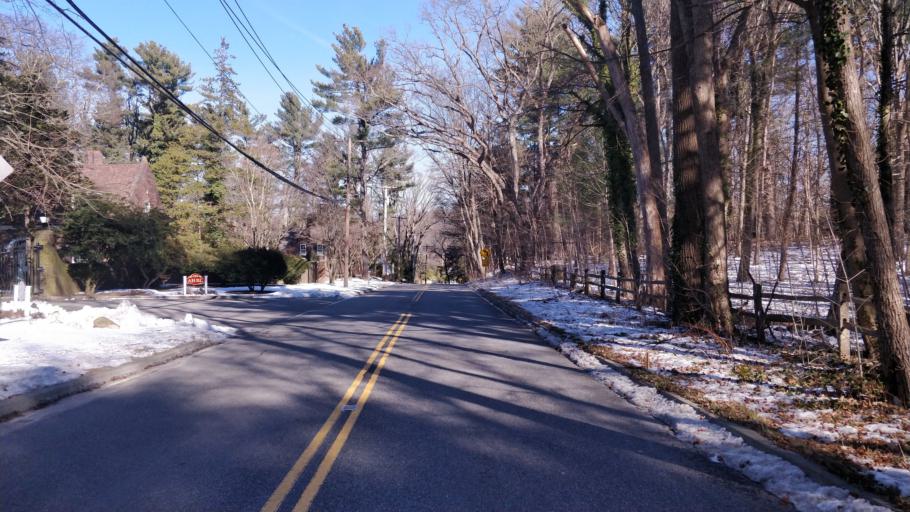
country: US
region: New York
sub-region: Nassau County
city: Brookville
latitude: 40.8081
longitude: -73.5797
